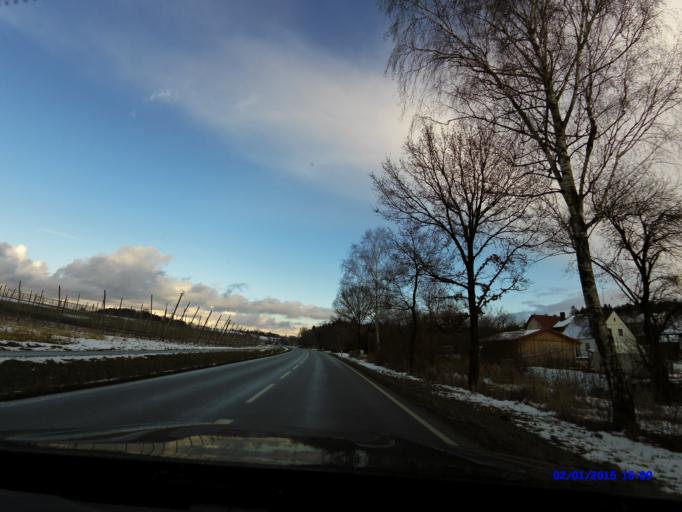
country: DE
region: Bavaria
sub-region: Lower Bavaria
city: Mainburg
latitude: 48.6300
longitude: 11.7497
